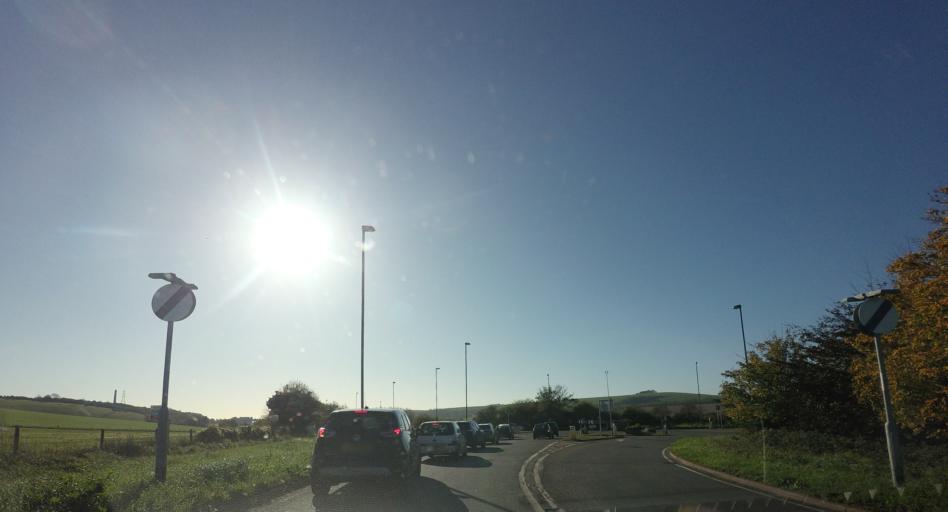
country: GB
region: England
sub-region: West Sussex
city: Steyning
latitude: 50.8753
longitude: -0.2995
